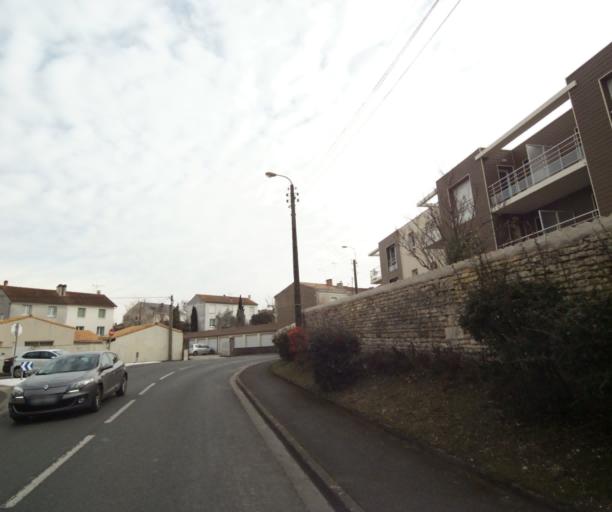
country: FR
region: Poitou-Charentes
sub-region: Departement des Deux-Sevres
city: Niort
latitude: 46.3164
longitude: -0.4540
